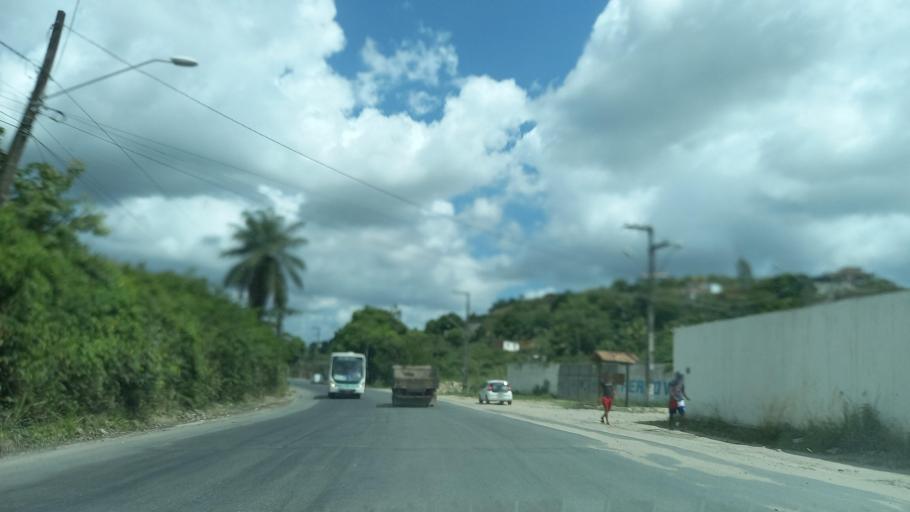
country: BR
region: Pernambuco
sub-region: Jaboatao Dos Guararapes
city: Jaboatao dos Guararapes
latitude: -8.1188
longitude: -35.0053
